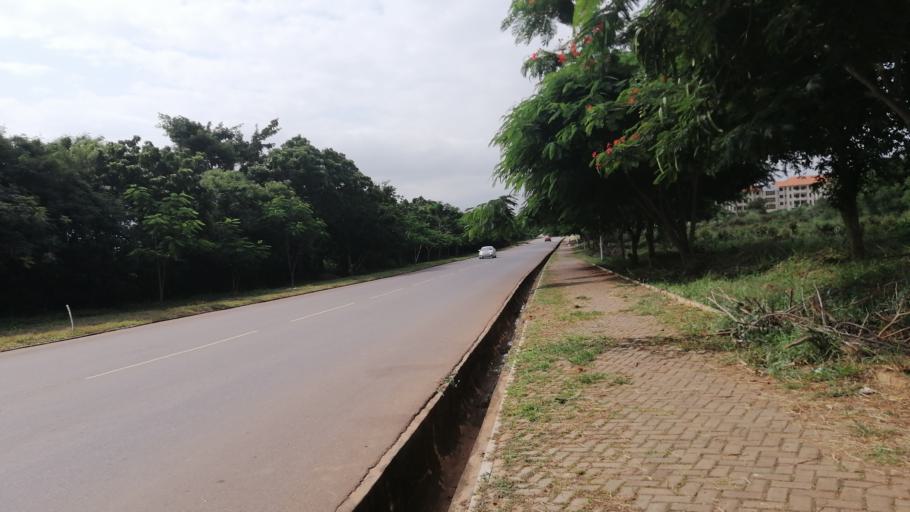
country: GH
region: Greater Accra
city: Medina Estates
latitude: 5.6601
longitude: -0.1826
